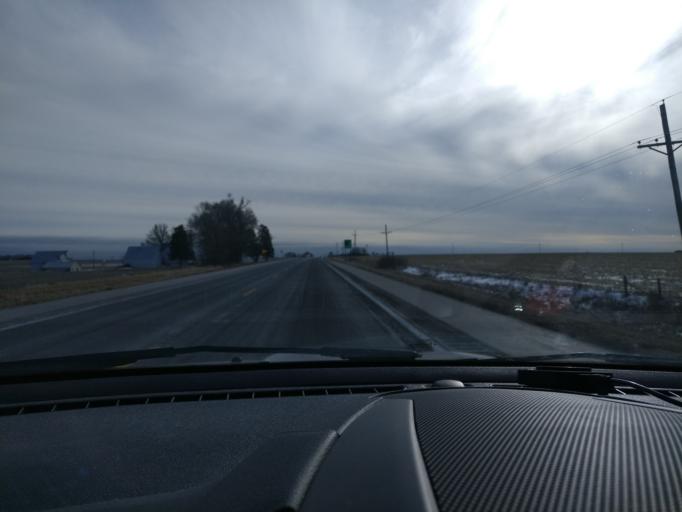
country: US
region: Nebraska
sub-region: Dodge County
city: Fremont
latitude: 41.3108
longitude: -96.5026
